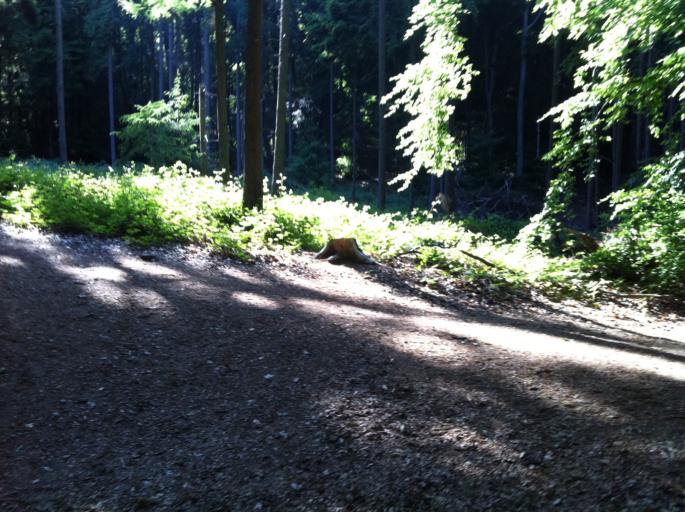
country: DE
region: Rheinland-Pfalz
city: Weiler
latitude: 49.9769
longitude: 7.8586
